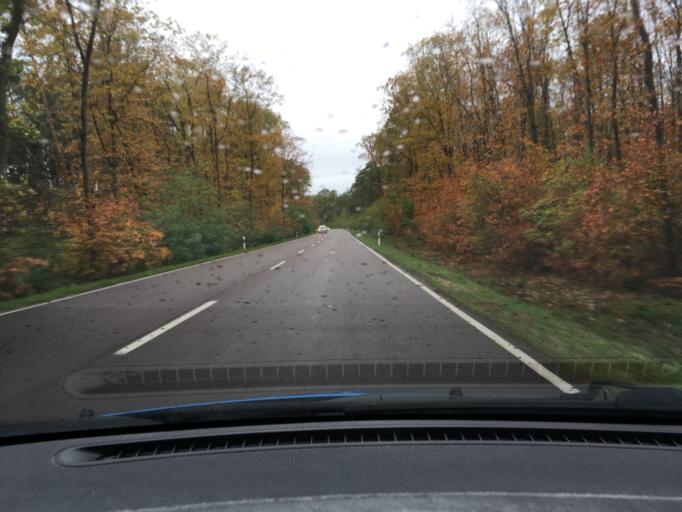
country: DE
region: Saxony-Anhalt
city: Klieken
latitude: 51.8932
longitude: 12.3334
